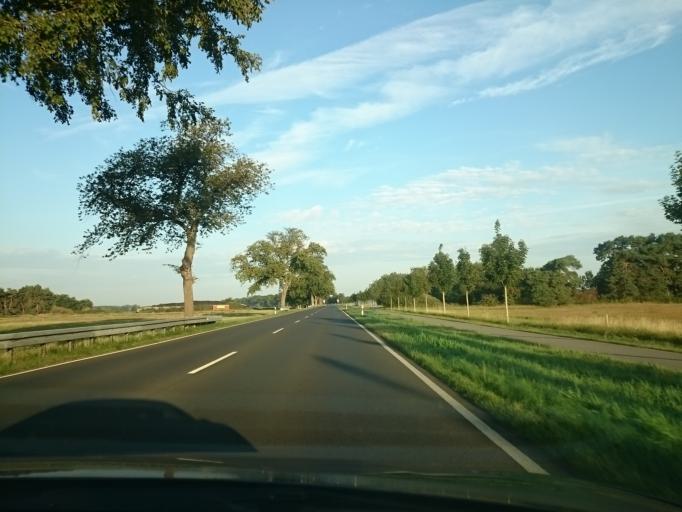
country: DE
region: Mecklenburg-Vorpommern
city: Ostseebad Zinnowitz
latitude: 54.0699
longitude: 13.8838
